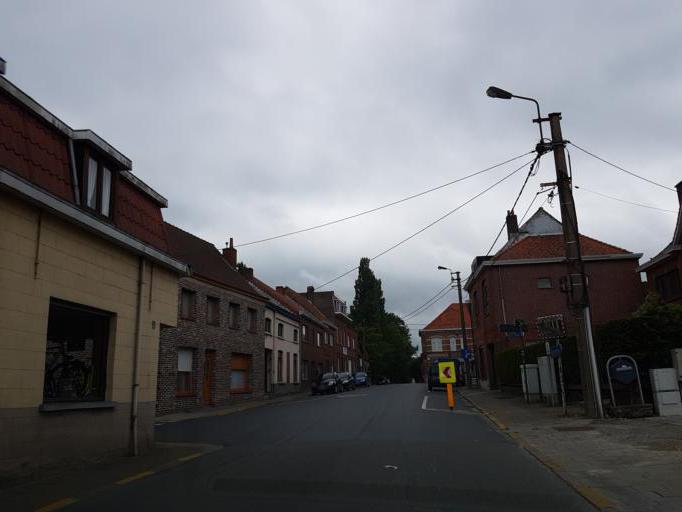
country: BE
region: Flanders
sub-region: Provincie Oost-Vlaanderen
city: Zomergem
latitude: 51.1143
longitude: 3.5601
